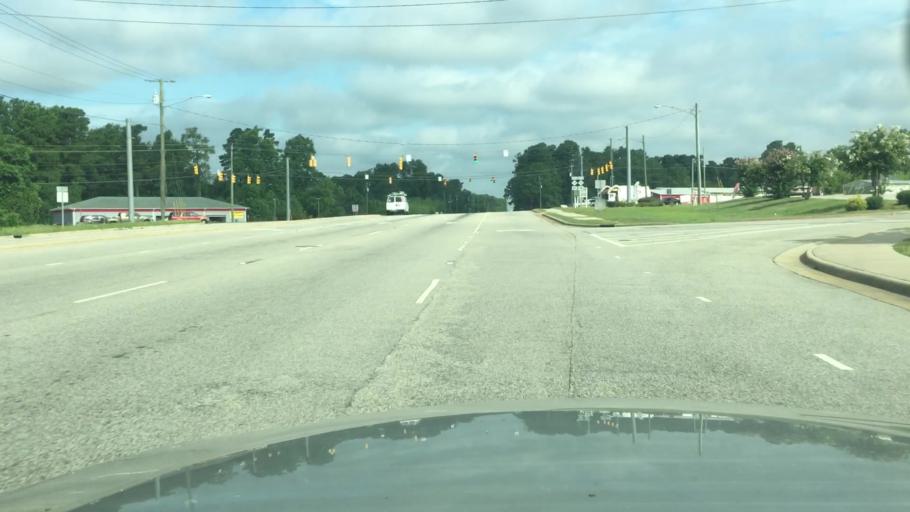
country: US
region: North Carolina
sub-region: Cumberland County
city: Hope Mills
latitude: 34.9949
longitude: -78.9665
